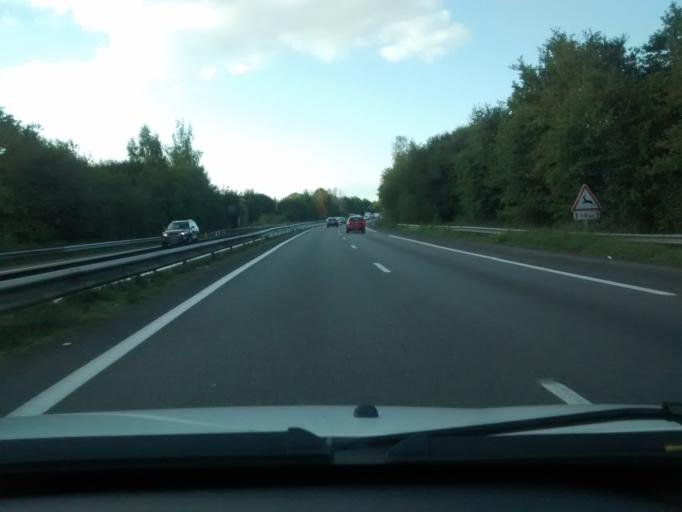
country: FR
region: Pays de la Loire
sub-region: Departement de la Loire-Atlantique
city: Orvault
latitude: 47.2804
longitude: -1.6025
